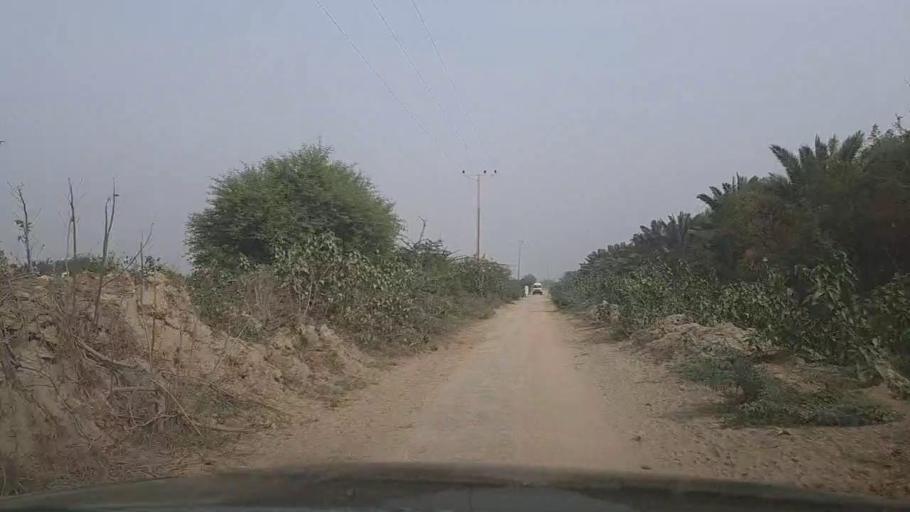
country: PK
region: Sindh
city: Mirpur Sakro
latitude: 24.5608
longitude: 67.7797
